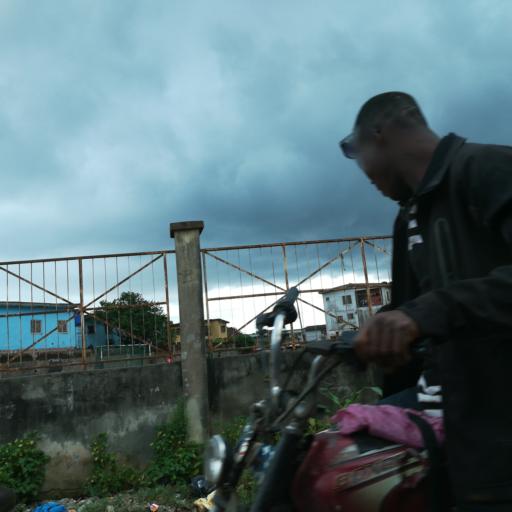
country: NG
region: Lagos
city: Agege
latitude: 6.6079
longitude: 3.3068
